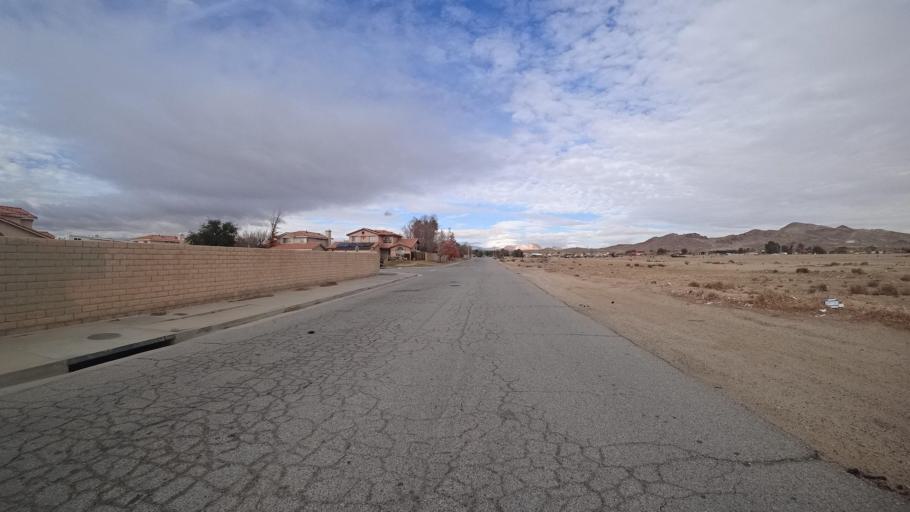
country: US
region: California
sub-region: Kern County
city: Rosamond
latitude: 34.8640
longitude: -118.2025
